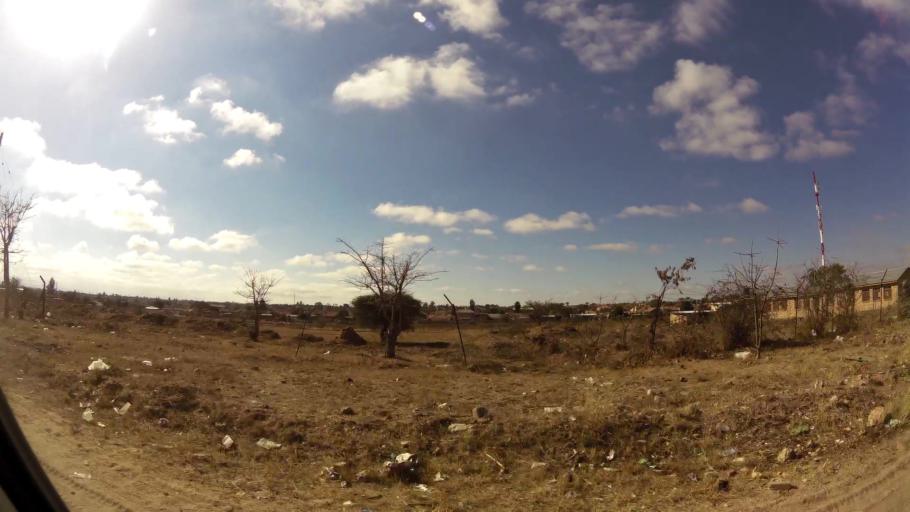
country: ZA
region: Limpopo
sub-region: Capricorn District Municipality
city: Polokwane
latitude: -23.8563
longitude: 29.3668
